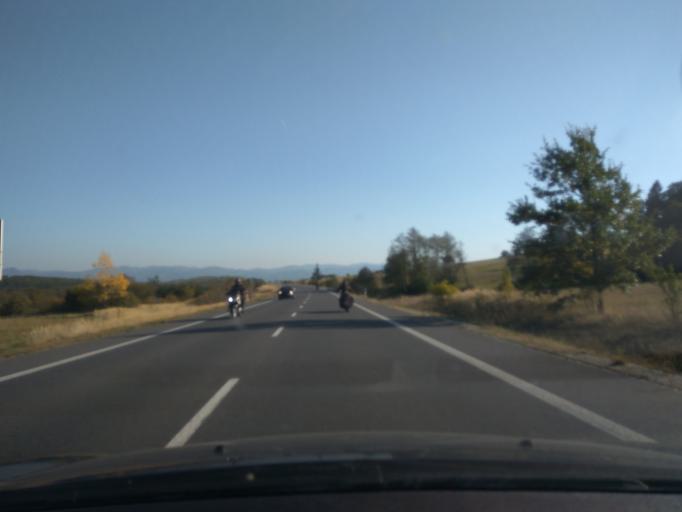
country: SK
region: Nitriansky
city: Handlova
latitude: 48.6418
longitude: 18.7706
